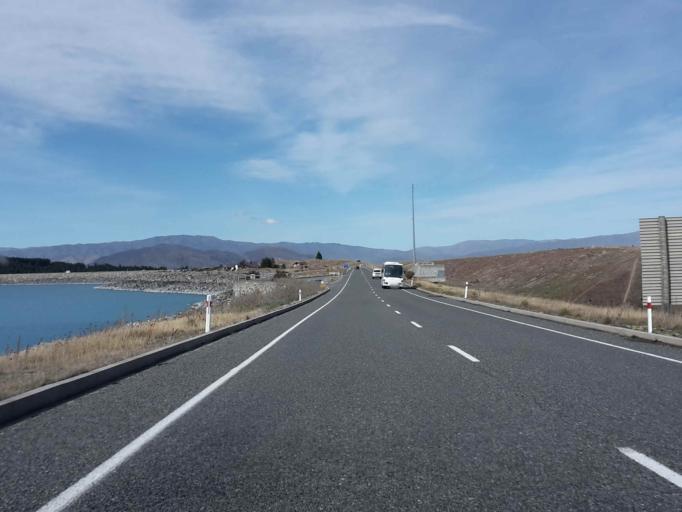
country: NZ
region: Canterbury
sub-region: Timaru District
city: Pleasant Point
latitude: -44.1874
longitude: 170.1334
